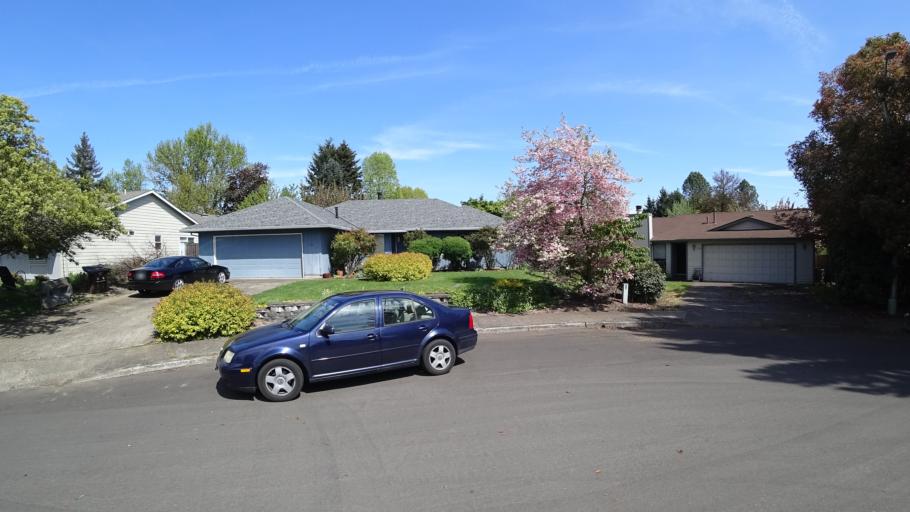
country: US
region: Oregon
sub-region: Washington County
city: Hillsboro
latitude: 45.5094
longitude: -122.9526
